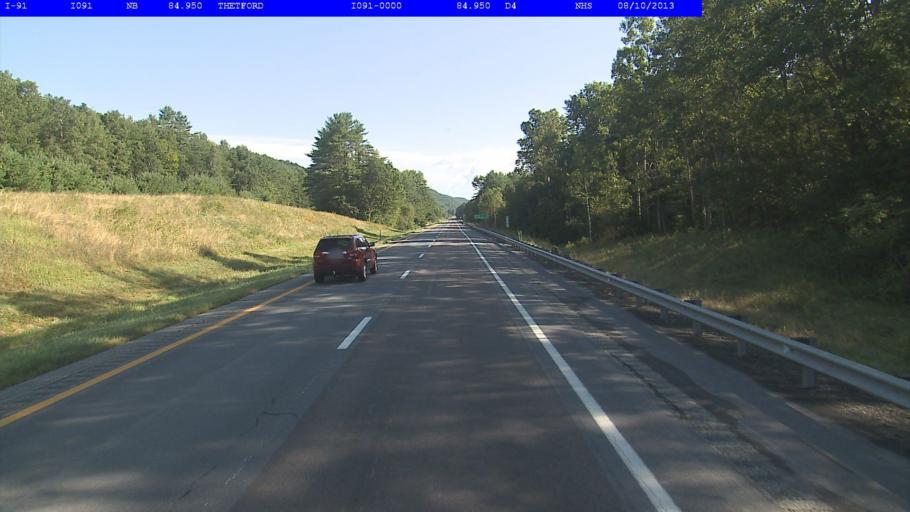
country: US
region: New Hampshire
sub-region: Grafton County
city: Lyme
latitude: 43.8222
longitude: -72.2103
